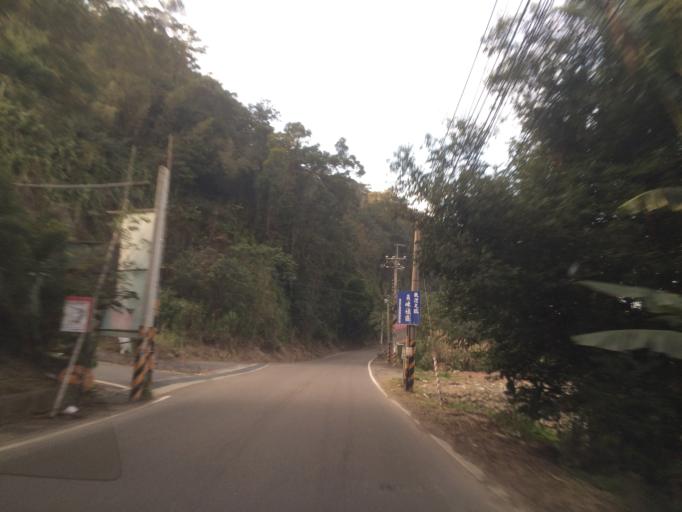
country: TW
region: Taiwan
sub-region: Hsinchu
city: Zhubei
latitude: 24.7007
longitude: 121.0966
